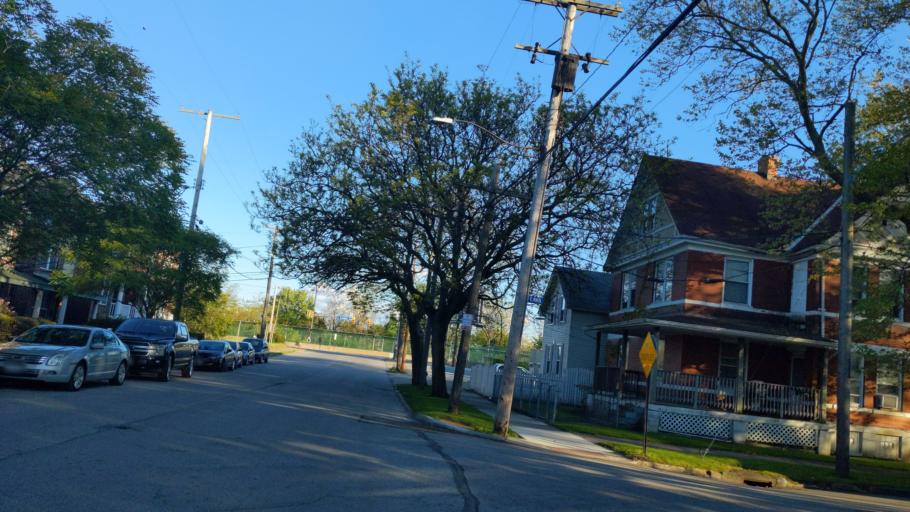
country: US
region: Ohio
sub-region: Cuyahoga County
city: Cleveland
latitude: 41.4771
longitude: -81.7261
